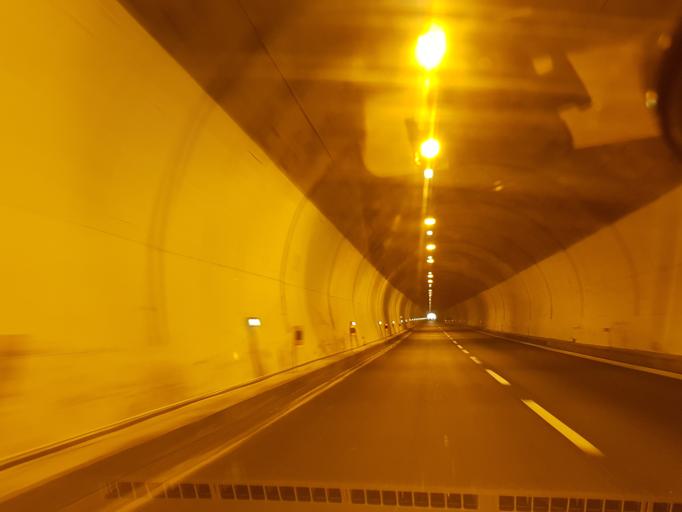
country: IT
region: Liguria
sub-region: Provincia di Genova
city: Manesseno
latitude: 44.4586
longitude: 8.9046
